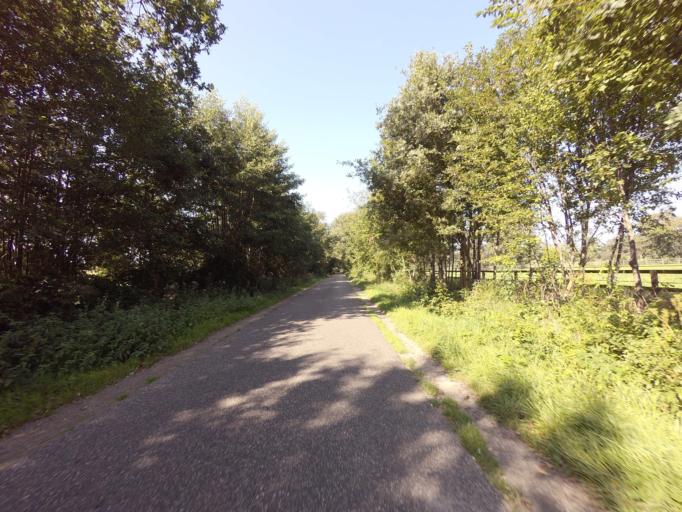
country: NL
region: Overijssel
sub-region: Gemeente Haaksbergen
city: Haaksbergen
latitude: 52.2018
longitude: 6.7789
